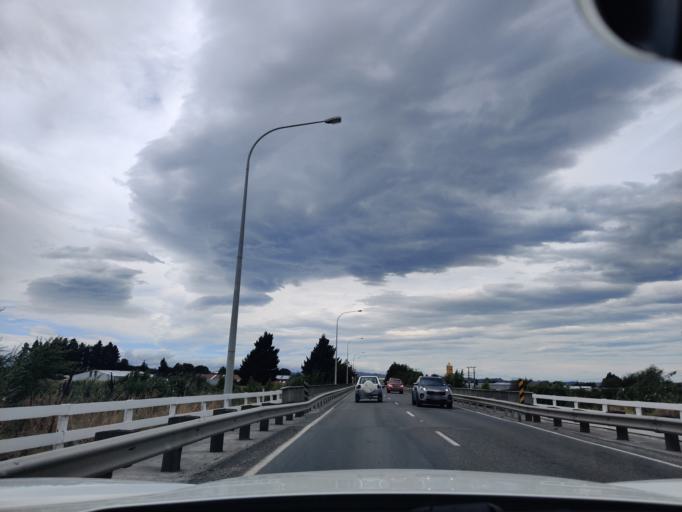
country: NZ
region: Wellington
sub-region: Masterton District
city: Masterton
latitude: -40.9651
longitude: 175.6085
